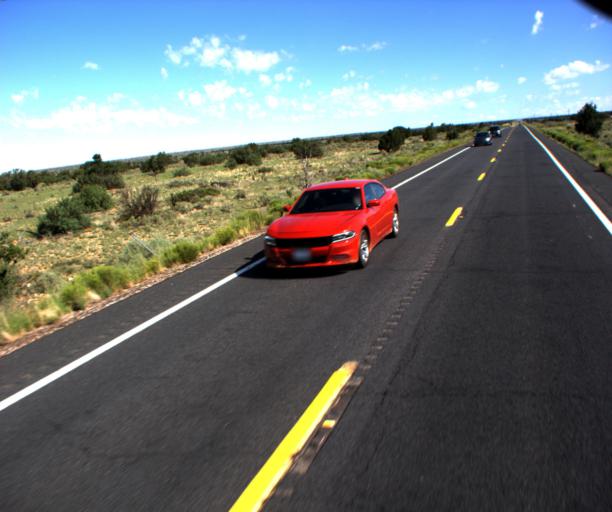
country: US
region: Arizona
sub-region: Coconino County
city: Grand Canyon Village
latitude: 35.7212
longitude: -112.1312
